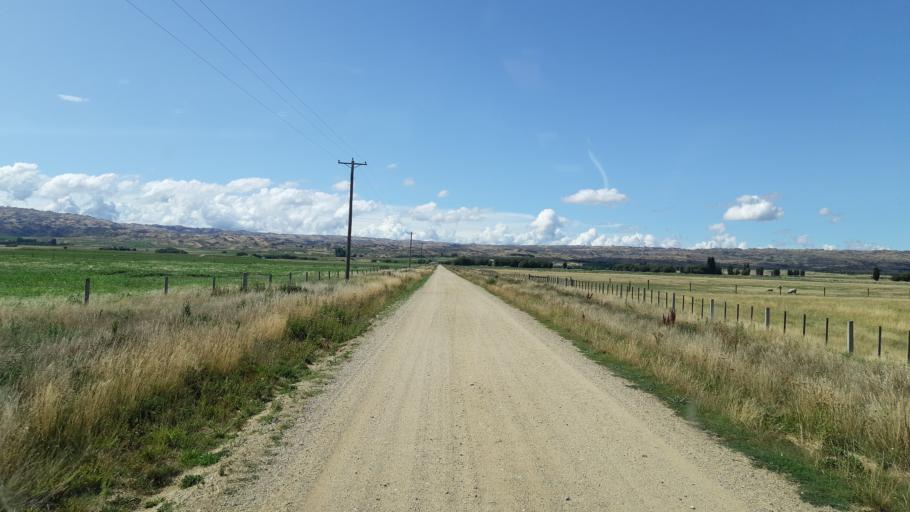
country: NZ
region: Otago
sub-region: Queenstown-Lakes District
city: Wanaka
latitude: -45.2079
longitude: 169.6654
